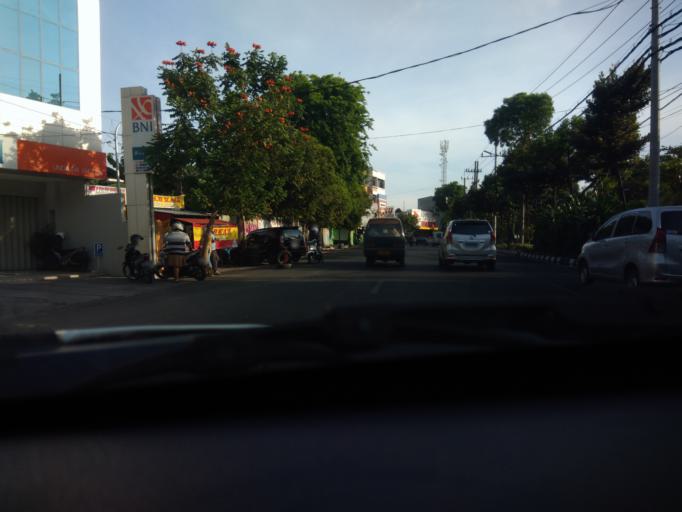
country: ID
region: East Java
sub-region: Kota Surabaya
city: Surabaya
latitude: -7.2529
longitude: 112.7445
